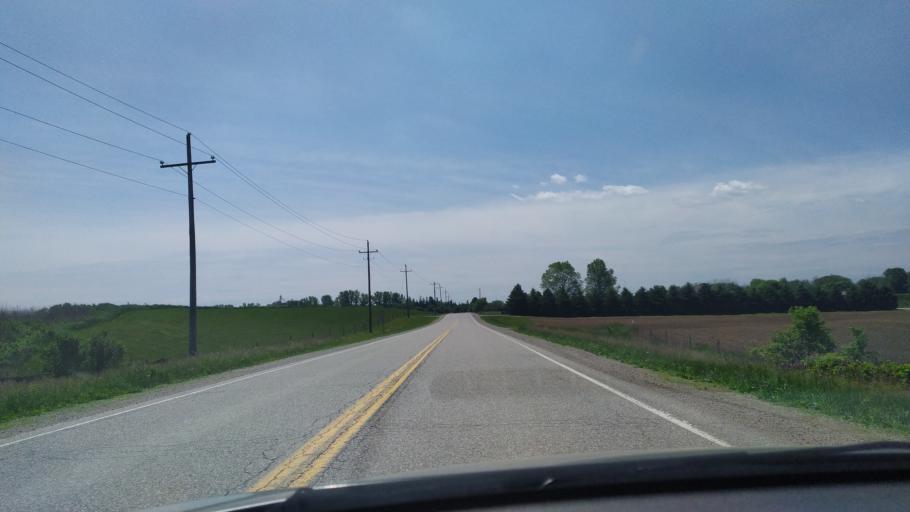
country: CA
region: Ontario
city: Ingersoll
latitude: 42.9991
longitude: -80.9573
